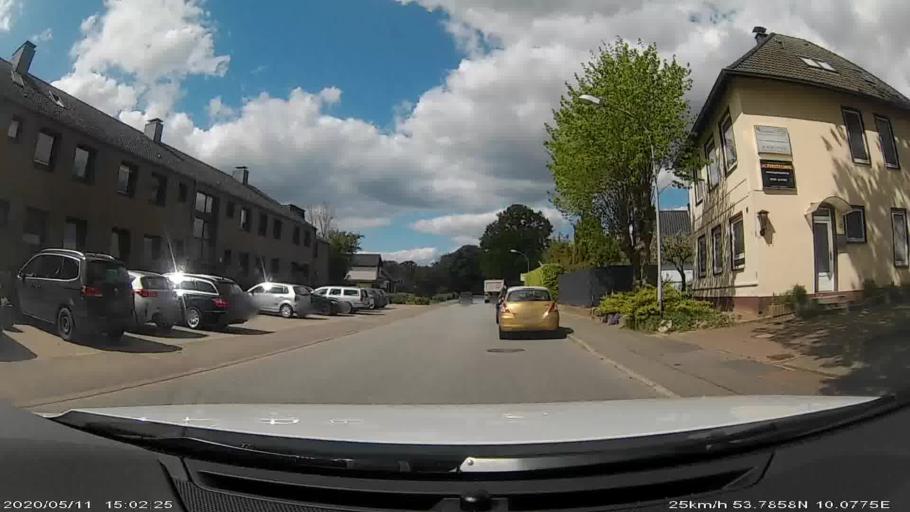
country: DE
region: Schleswig-Holstein
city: Huttblek
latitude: 53.7906
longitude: 10.0570
